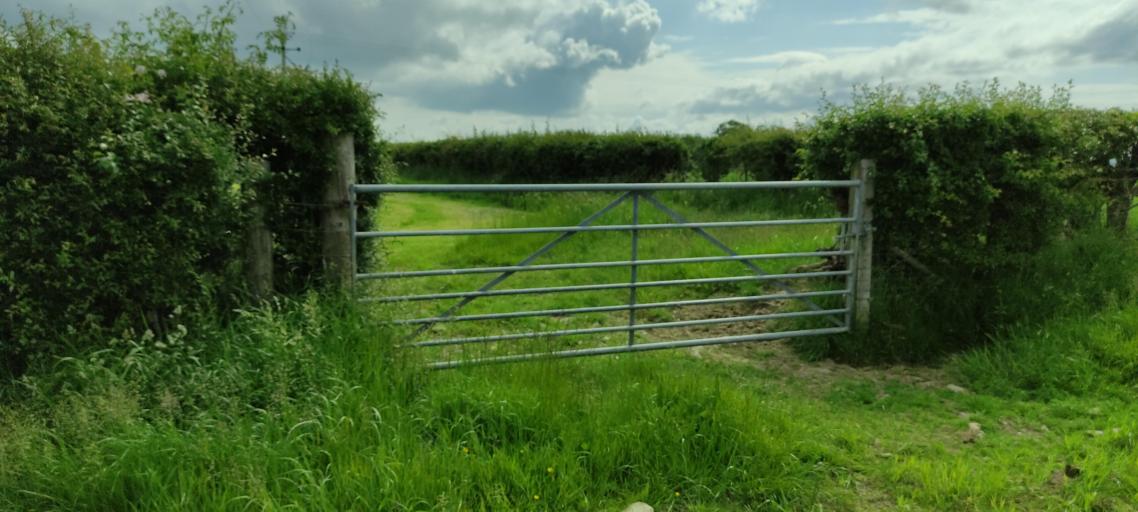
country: GB
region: England
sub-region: Cumbria
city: Cockermouth
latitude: 54.6855
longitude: -3.3851
